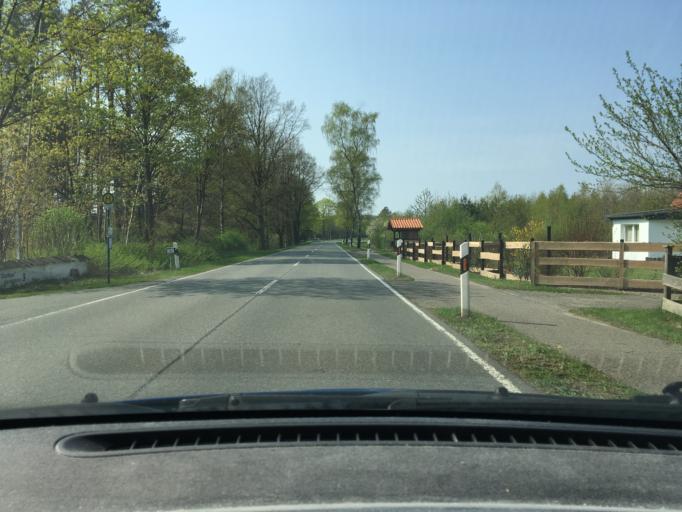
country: DE
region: Lower Saxony
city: Fassberg
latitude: 52.8776
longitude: 10.1985
